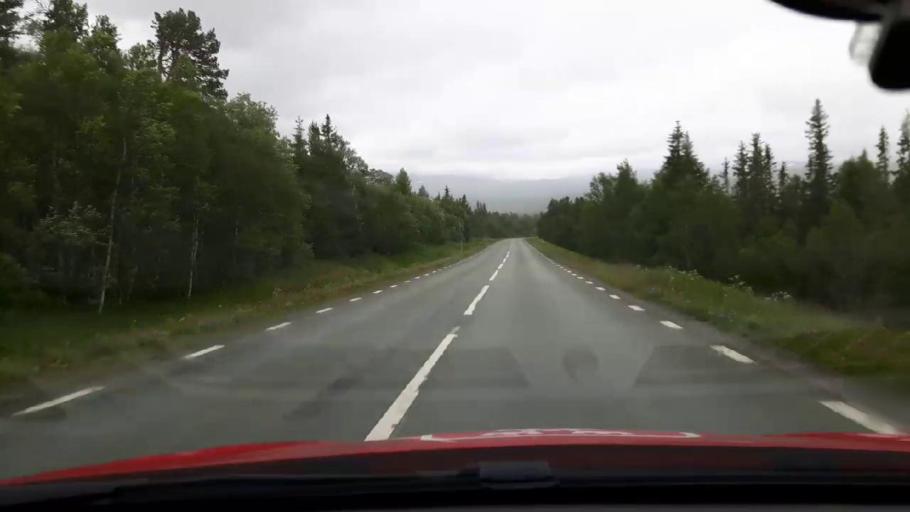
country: NO
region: Nord-Trondelag
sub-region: Meraker
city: Meraker
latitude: 63.2969
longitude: 12.1139
